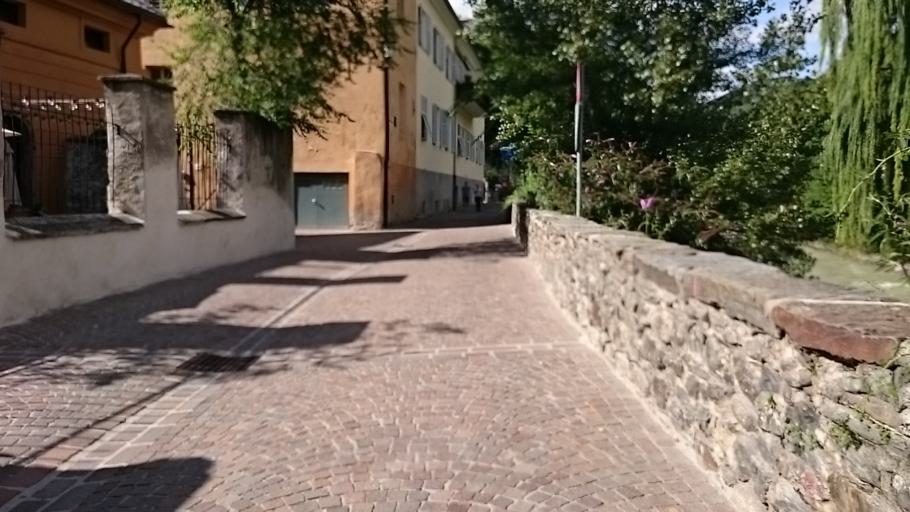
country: IT
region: Trentino-Alto Adige
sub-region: Bolzano
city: Bressanone
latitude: 46.7172
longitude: 11.6586
